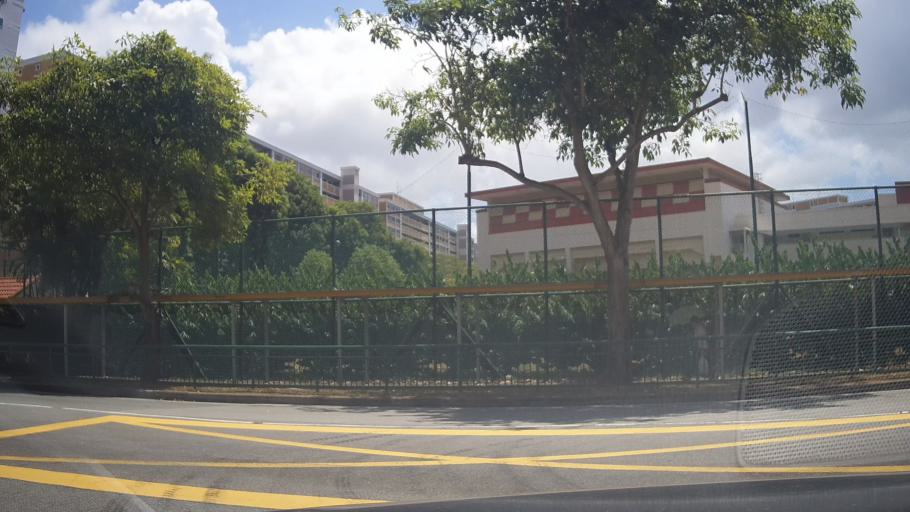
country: SG
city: Singapore
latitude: 1.3618
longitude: 103.9553
